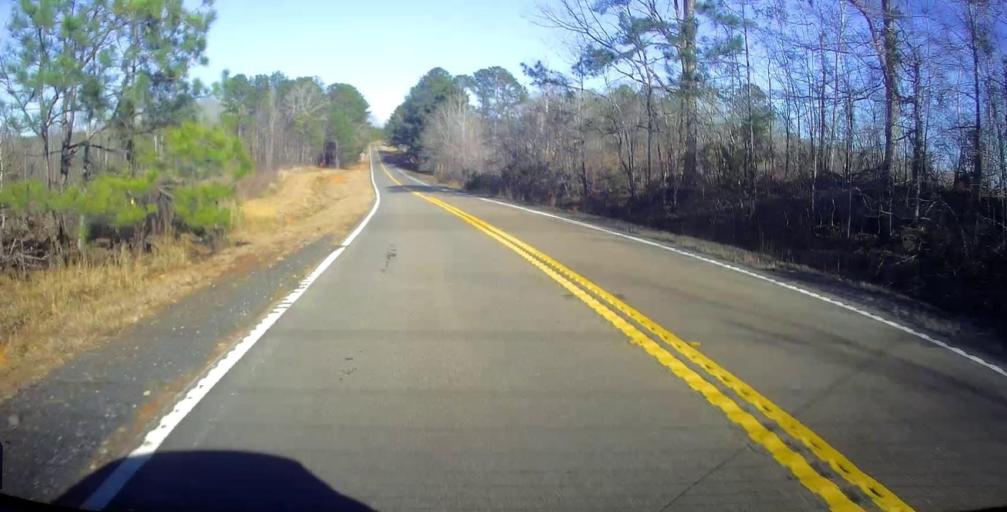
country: US
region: Georgia
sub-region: Talbot County
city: Talbotton
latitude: 32.6480
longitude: -84.3994
